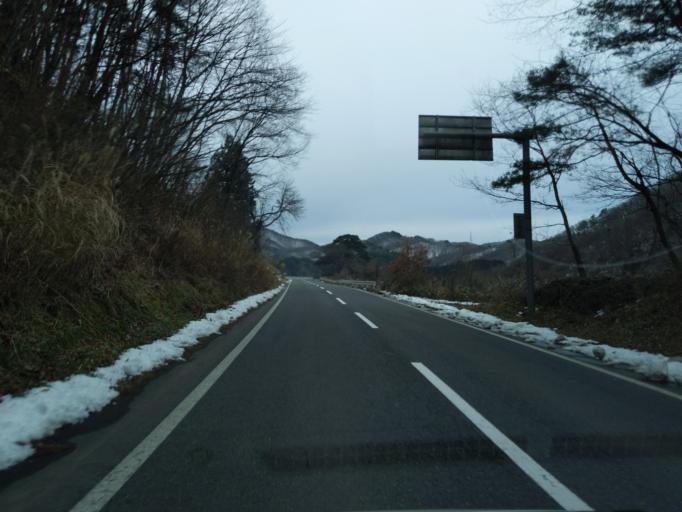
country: JP
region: Iwate
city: Mizusawa
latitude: 39.1119
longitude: 141.2669
